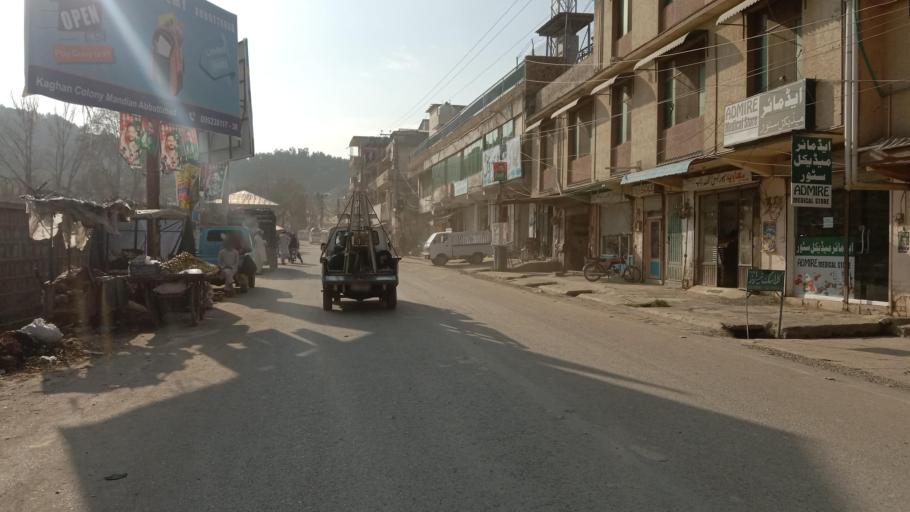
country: PK
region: Khyber Pakhtunkhwa
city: Abbottabad
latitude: 34.1977
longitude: 73.2309
